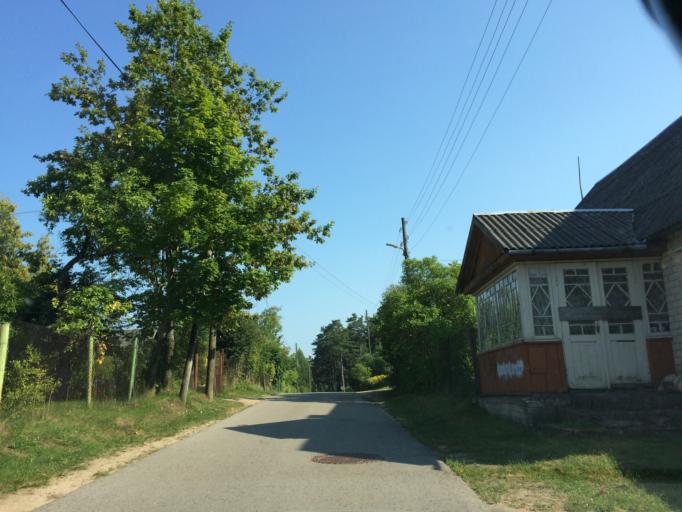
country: LV
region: Aglona
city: Aglona
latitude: 56.1319
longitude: 27.0035
